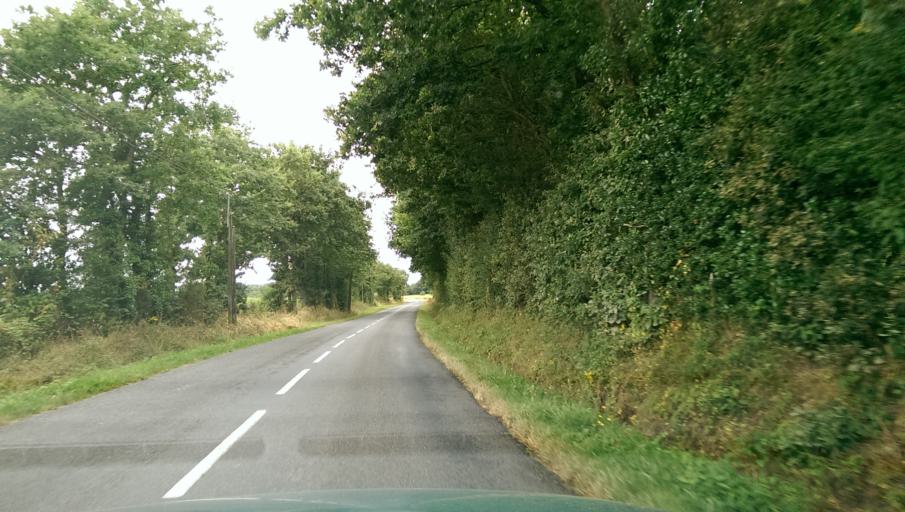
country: FR
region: Pays de la Loire
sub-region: Departement de la Loire-Atlantique
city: La Planche
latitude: 46.9990
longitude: -1.3885
